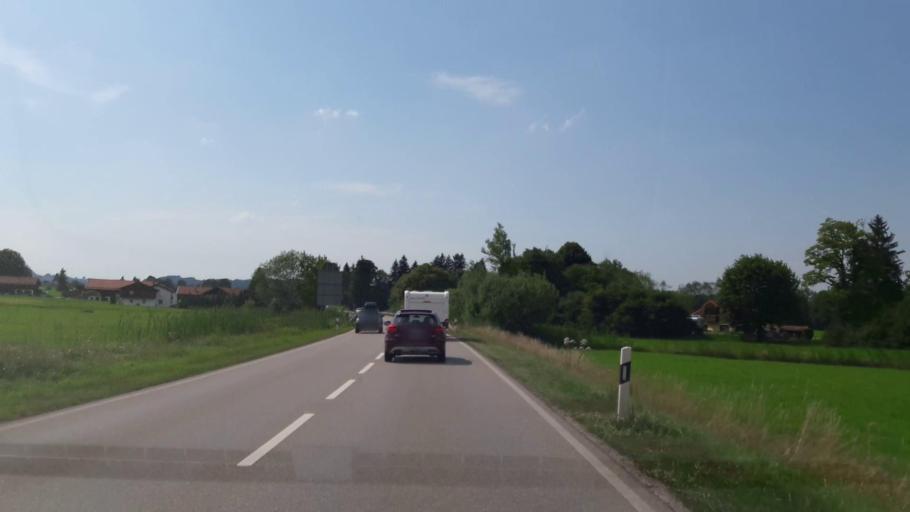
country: DE
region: Bavaria
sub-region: Upper Bavaria
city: Teisendorf
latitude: 47.8490
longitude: 12.8090
